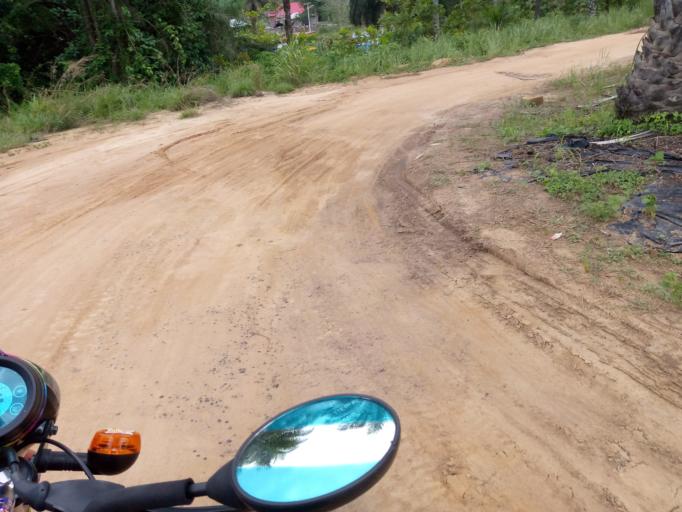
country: SL
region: Western Area
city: Waterloo
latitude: 8.3412
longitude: -13.0152
